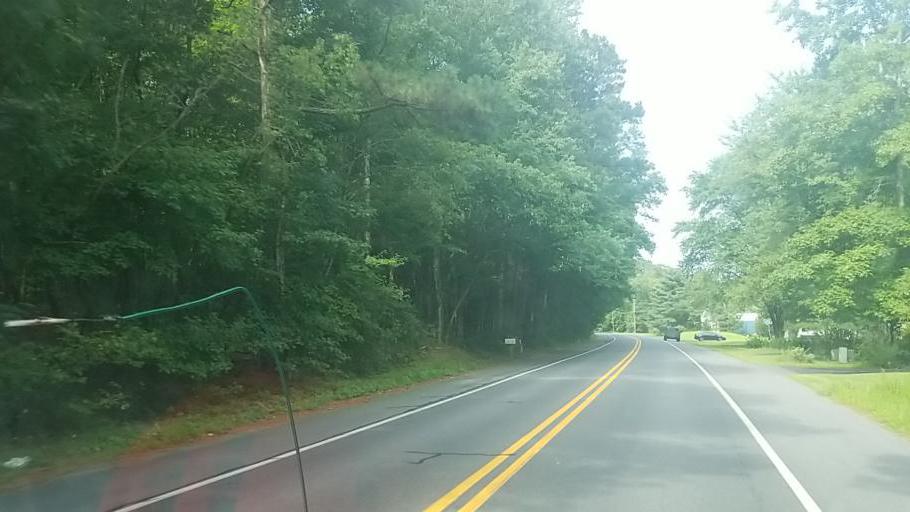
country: US
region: Delaware
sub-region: Sussex County
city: Long Neck
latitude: 38.5446
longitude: -75.1715
